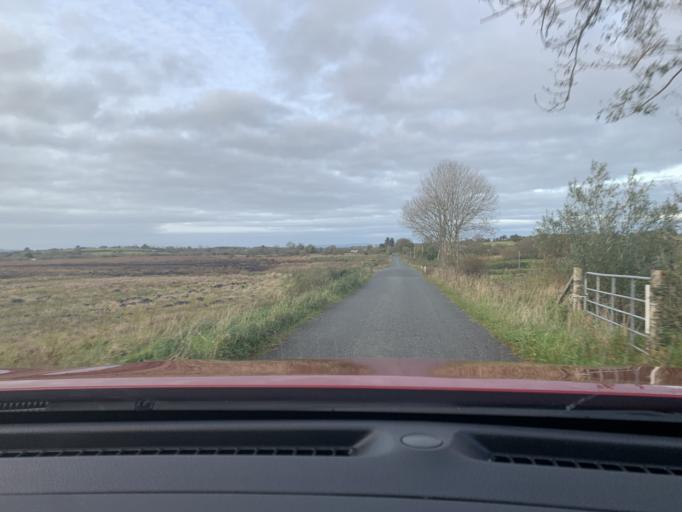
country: IE
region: Connaught
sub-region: Roscommon
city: Ballaghaderreen
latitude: 53.9935
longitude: -8.6095
